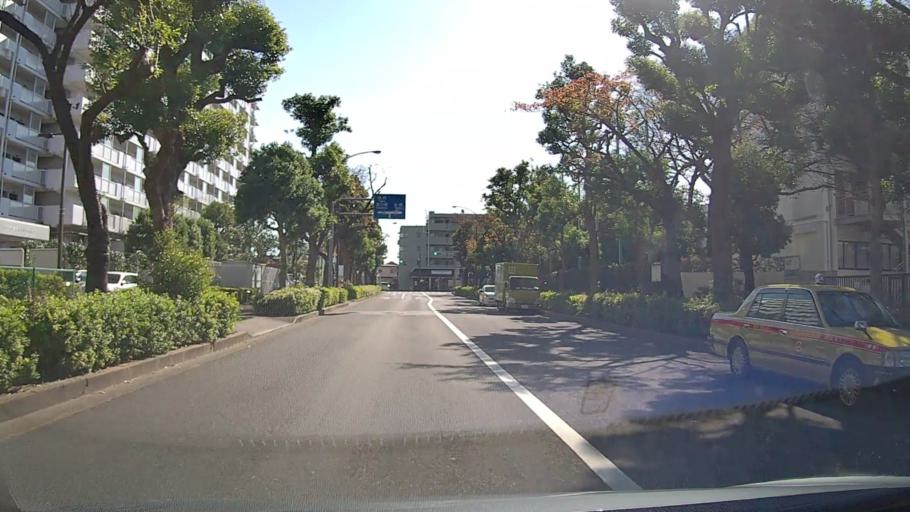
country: JP
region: Saitama
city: Wako
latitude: 35.7549
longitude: 139.6267
